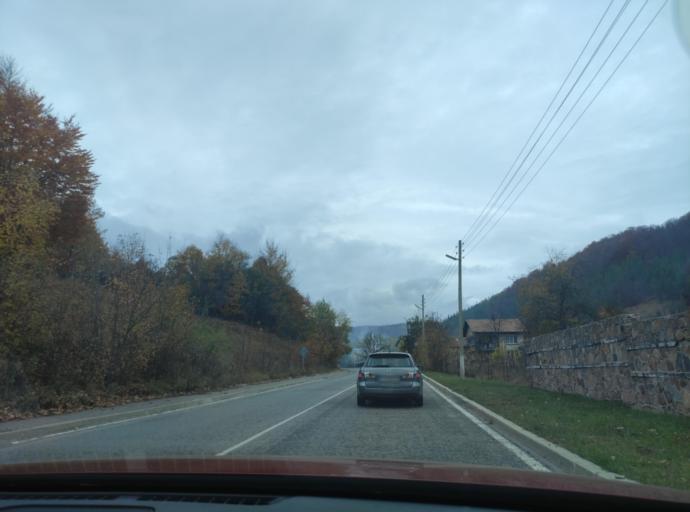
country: BG
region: Sofiya
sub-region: Obshtina Godech
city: Godech
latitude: 43.0849
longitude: 23.1026
